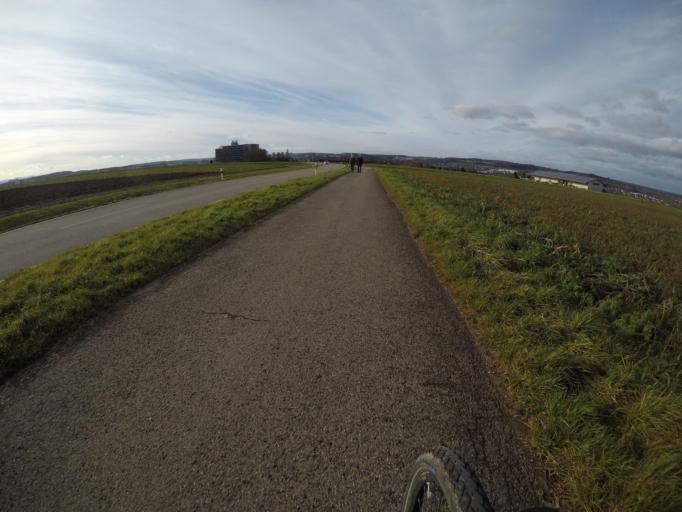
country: DE
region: Baden-Wuerttemberg
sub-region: Regierungsbezirk Stuttgart
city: Oberboihingen
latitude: 48.6305
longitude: 9.3648
